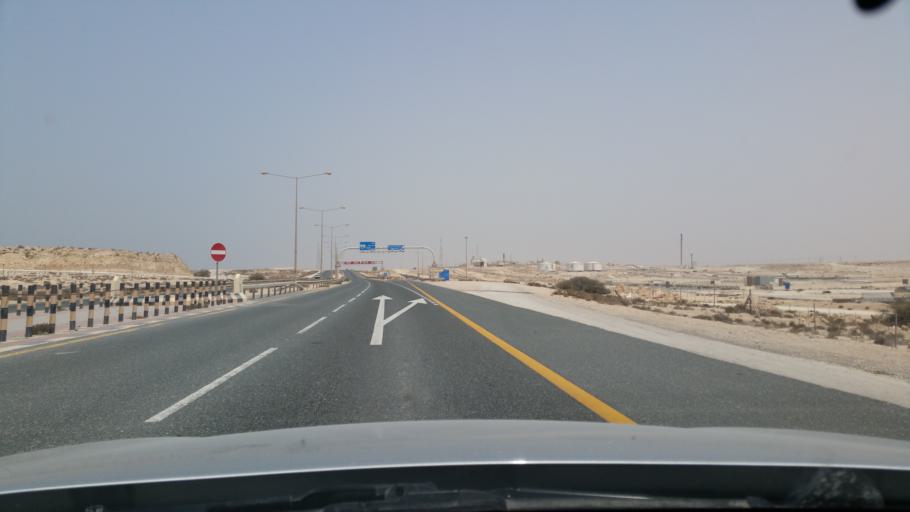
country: QA
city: Umm Bab
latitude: 25.2744
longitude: 50.7928
